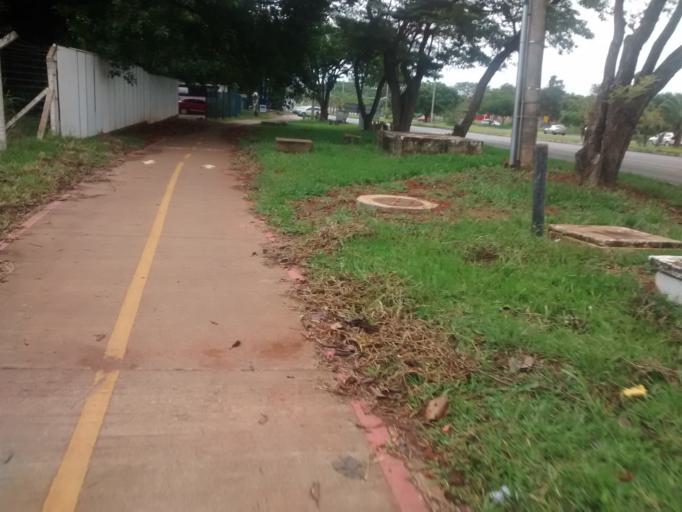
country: BR
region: Federal District
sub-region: Brasilia
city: Brasilia
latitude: -15.7589
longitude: -47.8752
